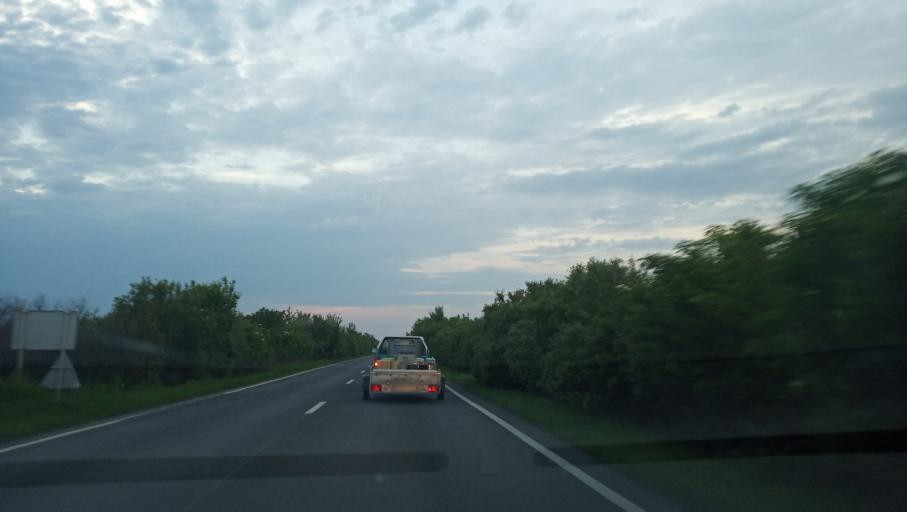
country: RO
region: Timis
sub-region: Comuna Voiteg
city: Voiteg
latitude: 45.5086
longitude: 21.2376
